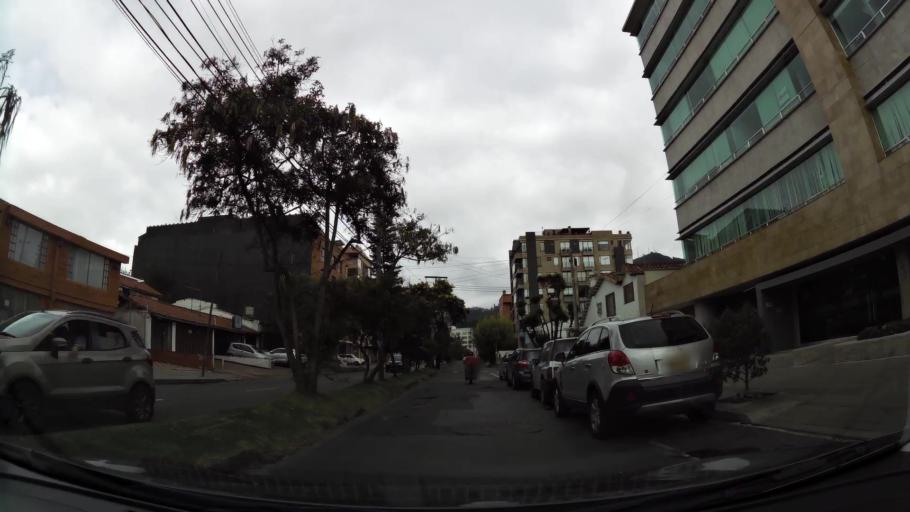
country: CO
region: Bogota D.C.
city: Barrio San Luis
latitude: 4.6885
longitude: -74.0464
